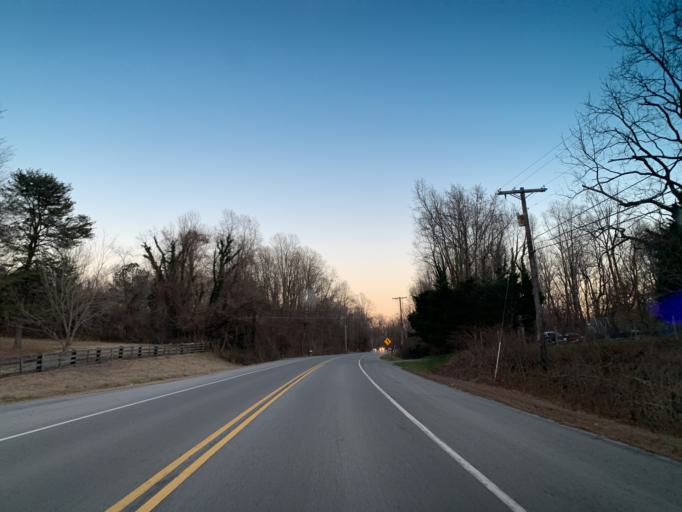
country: US
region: Maryland
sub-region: Calvert County
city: Prince Frederick
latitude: 38.5577
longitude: -76.5299
